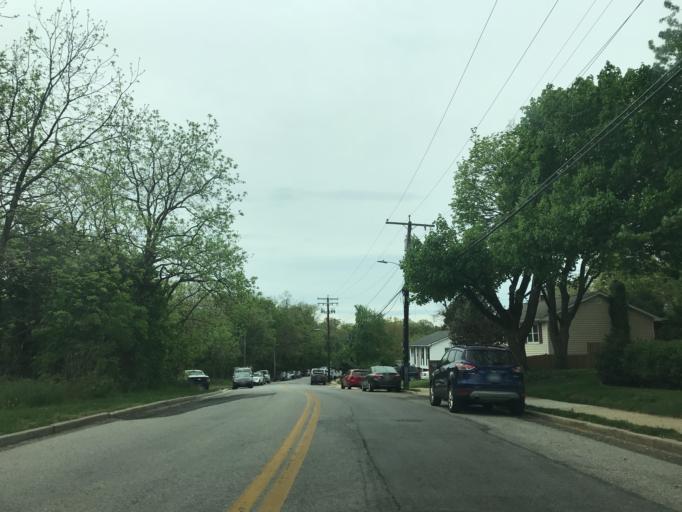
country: US
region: Maryland
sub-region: Baltimore County
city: Catonsville
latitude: 39.2671
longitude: -76.7323
